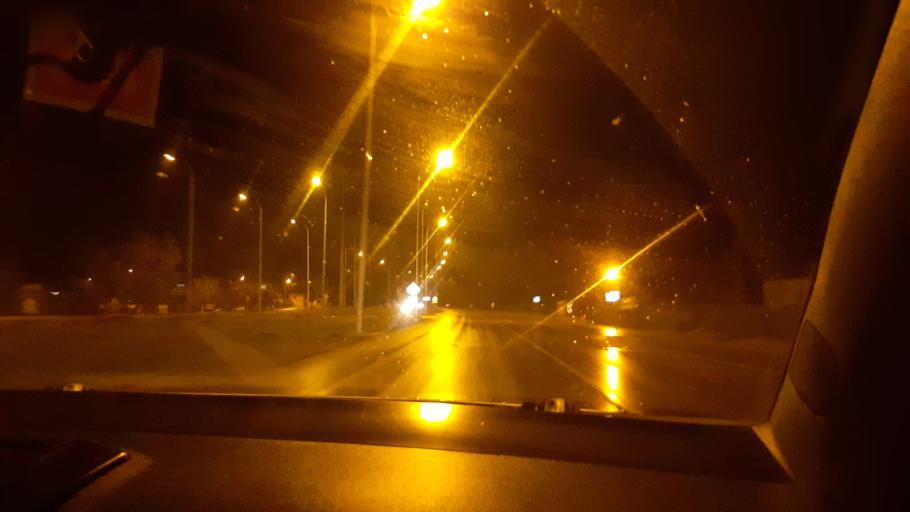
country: TR
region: Hatay
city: Aktepe
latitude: 36.7311
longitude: 36.5241
